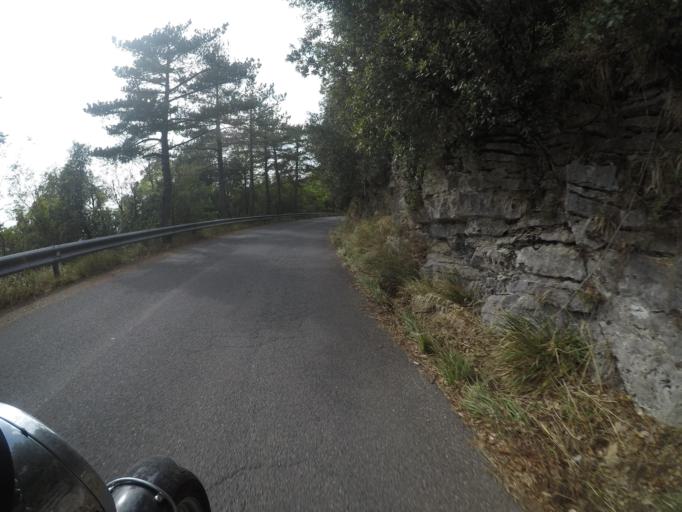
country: IT
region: Tuscany
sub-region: Provincia di Massa-Carrara
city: Fosdinovo
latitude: 44.1208
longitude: 10.0820
